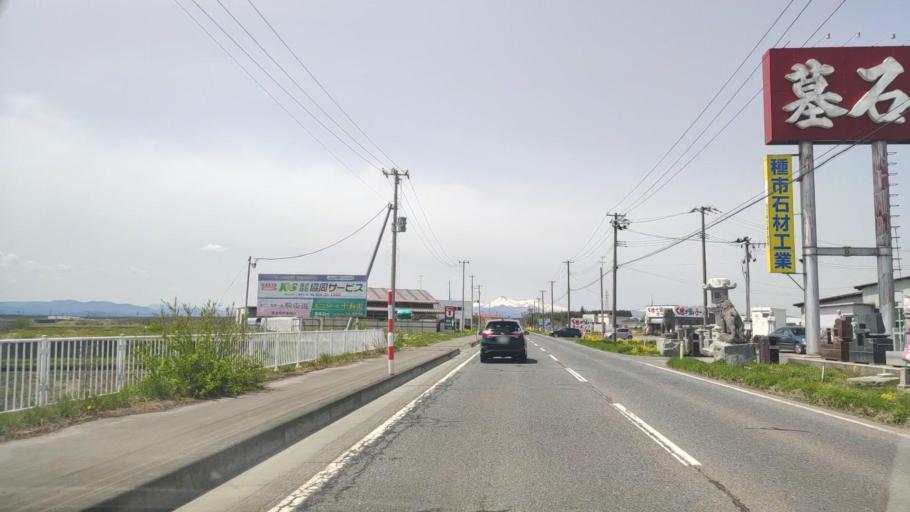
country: JP
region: Aomori
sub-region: Misawa Shi
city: Inuotose
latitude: 40.6112
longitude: 141.2698
